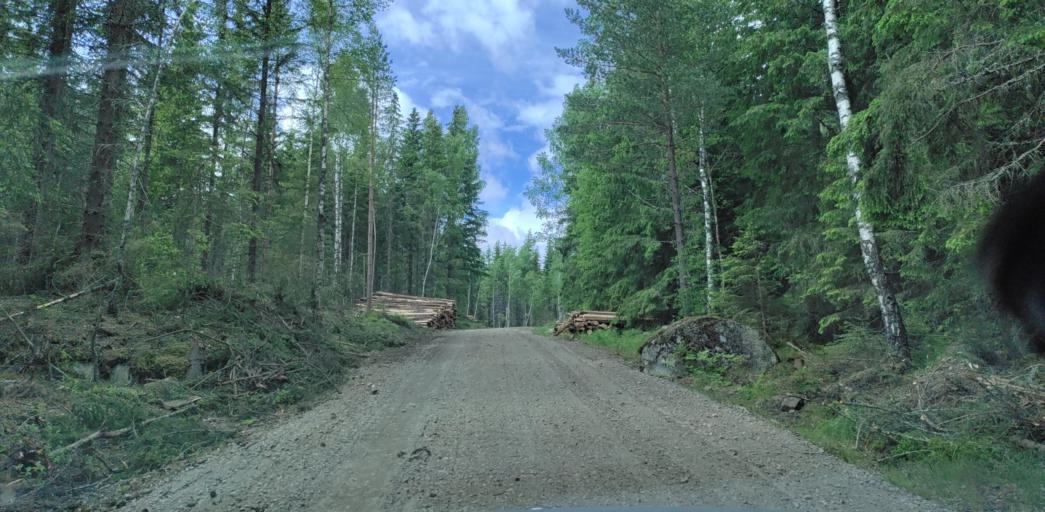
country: SE
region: Vaermland
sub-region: Munkfors Kommun
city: Munkfors
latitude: 59.9694
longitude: 13.4025
